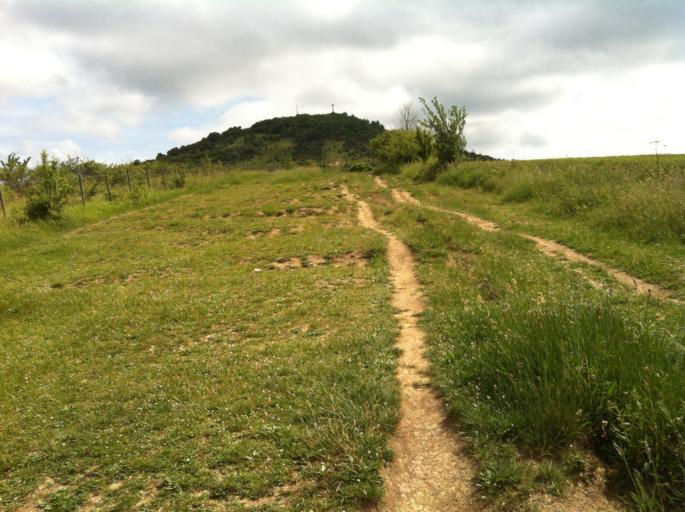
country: ES
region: Basque Country
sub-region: Provincia de Alava
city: Gasteiz / Vitoria
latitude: 42.8228
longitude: -2.6613
